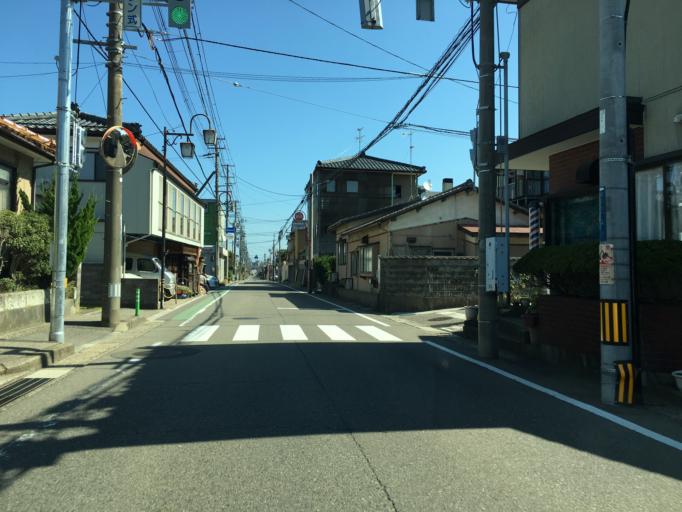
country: JP
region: Niigata
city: Niigata-shi
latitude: 37.9009
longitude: 138.9983
